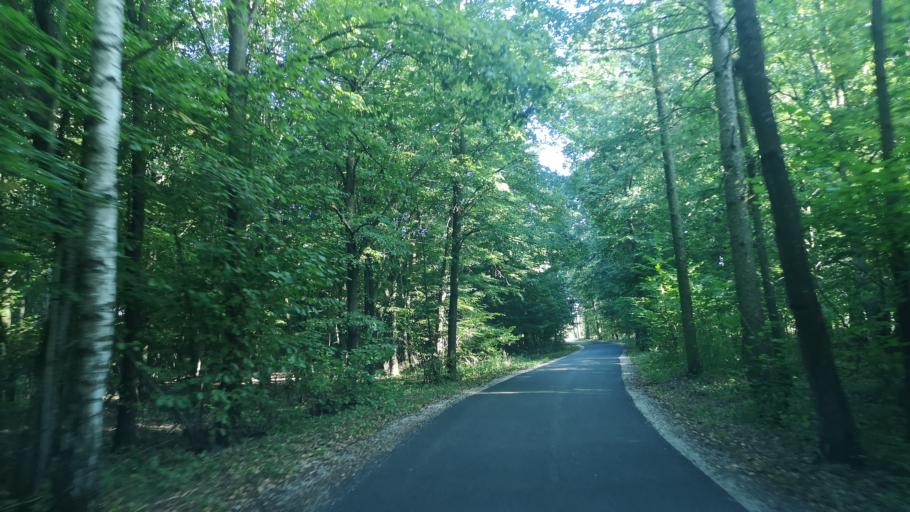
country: PL
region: Kujawsko-Pomorskie
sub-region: Powiat swiecki
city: Warlubie
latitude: 53.4764
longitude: 18.6339
